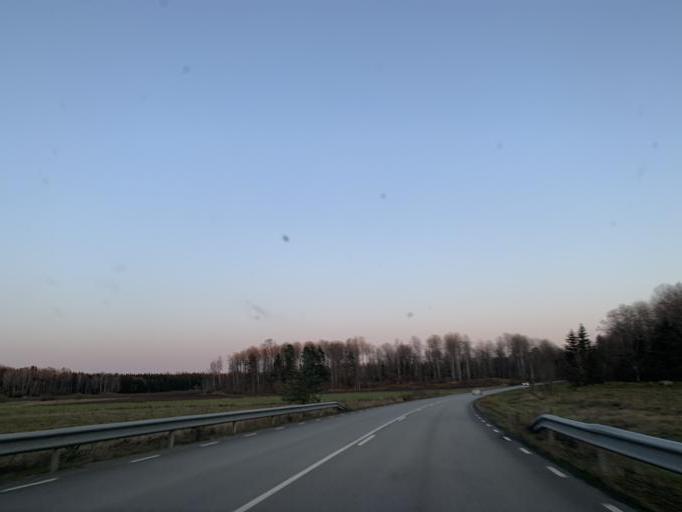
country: SE
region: OErebro
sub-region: Orebro Kommun
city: Hovsta
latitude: 59.3137
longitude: 15.2780
